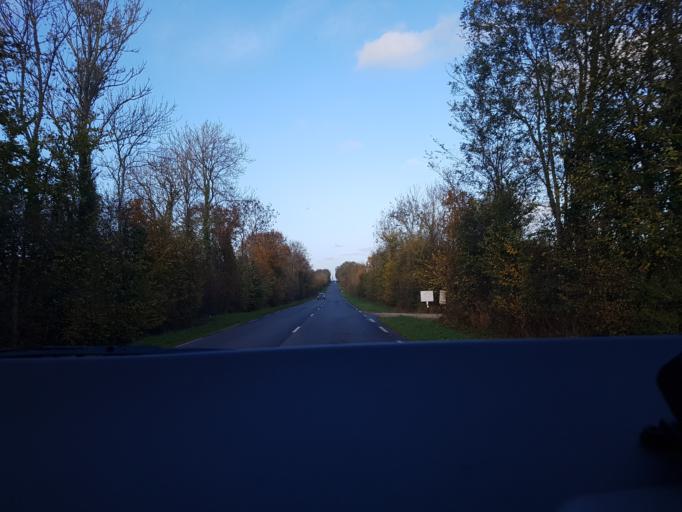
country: FR
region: Lower Normandy
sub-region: Departement du Calvados
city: Troarn
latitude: 49.2042
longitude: -0.1240
